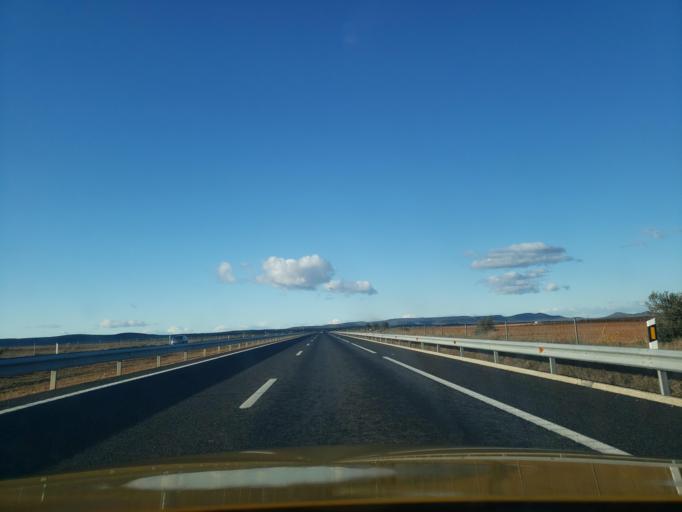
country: ES
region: Castille-La Mancha
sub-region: Province of Toledo
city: Turleque
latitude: 39.5560
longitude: -3.6785
